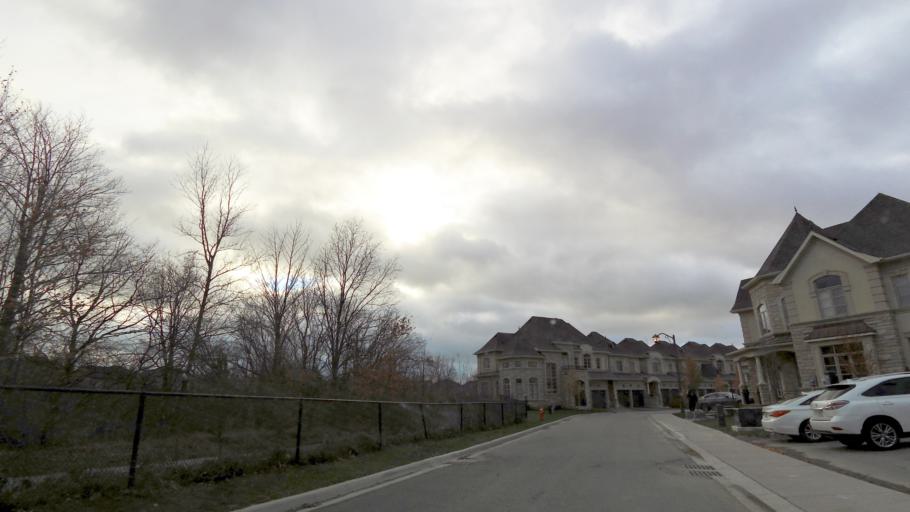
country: CA
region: Ontario
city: Burlington
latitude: 43.4284
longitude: -79.7786
